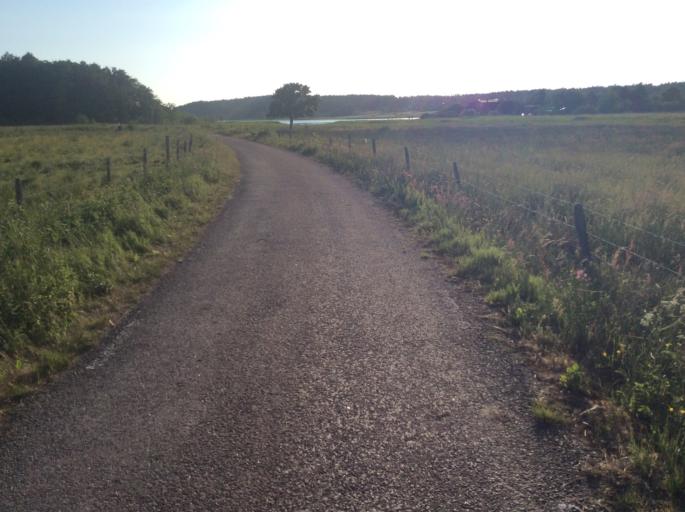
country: SE
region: Vaestra Goetaland
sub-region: Goteborg
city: Torslanda
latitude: 57.7973
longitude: 11.8585
